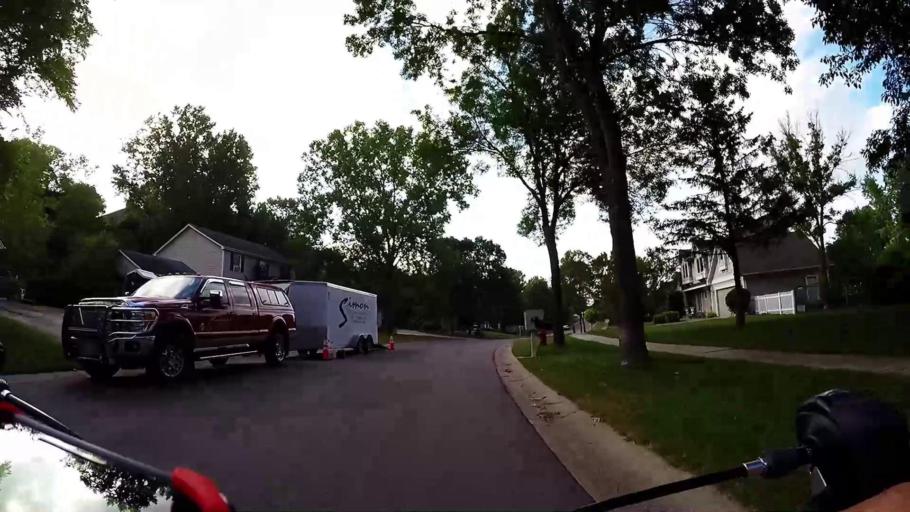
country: US
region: Minnesota
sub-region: Hennepin County
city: Eden Prairie
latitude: 44.8842
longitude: -93.4835
